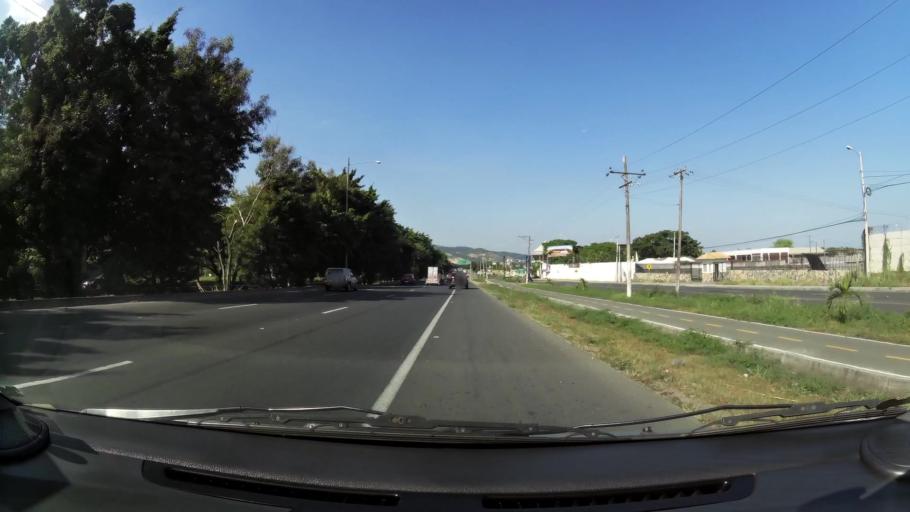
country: EC
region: Guayas
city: Santa Lucia
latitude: -2.1855
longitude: -80.0080
